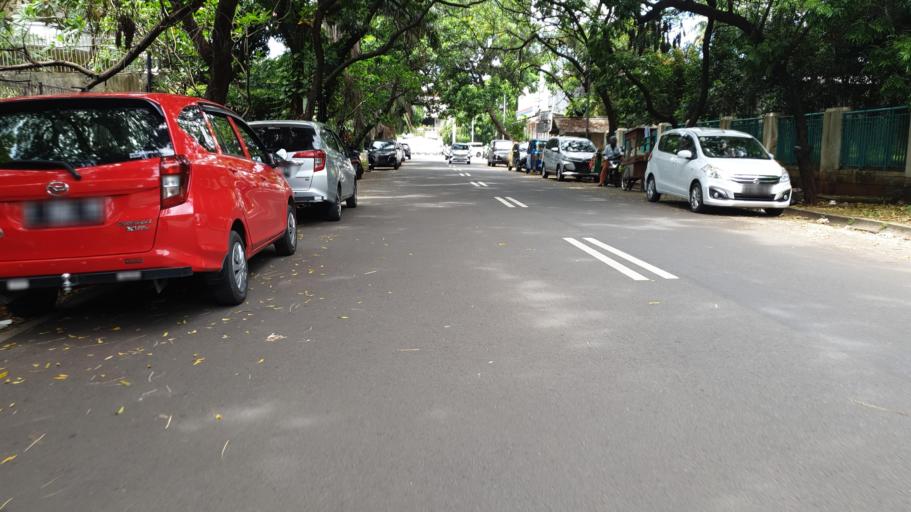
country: ID
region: Banten
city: South Tangerang
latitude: -6.2748
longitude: 106.7834
